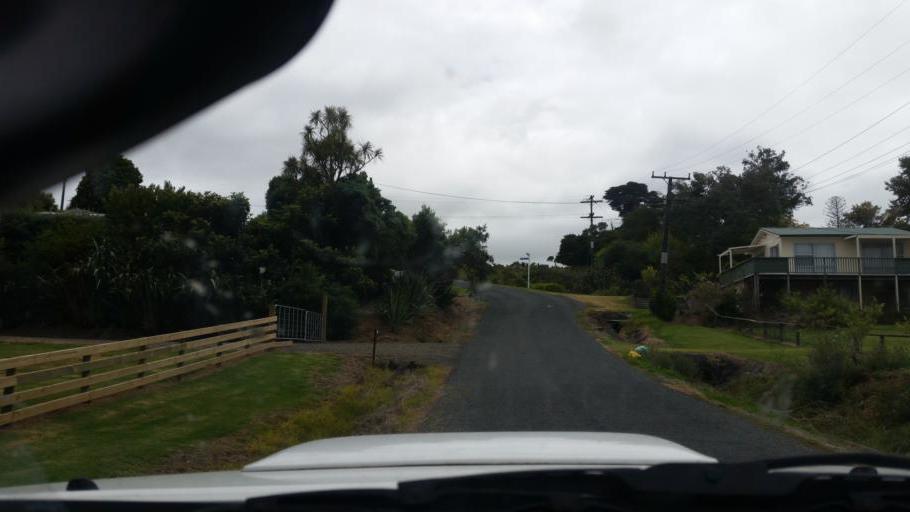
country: NZ
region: Auckland
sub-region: Auckland
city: Wellsford
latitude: -36.1581
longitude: 174.2386
